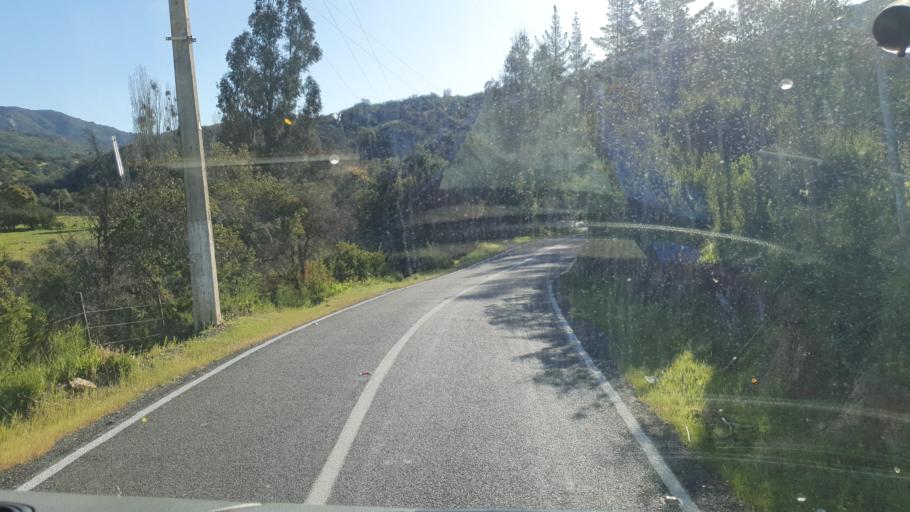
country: CL
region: Valparaiso
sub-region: Provincia de Marga Marga
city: Limache
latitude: -33.1959
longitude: -71.2167
